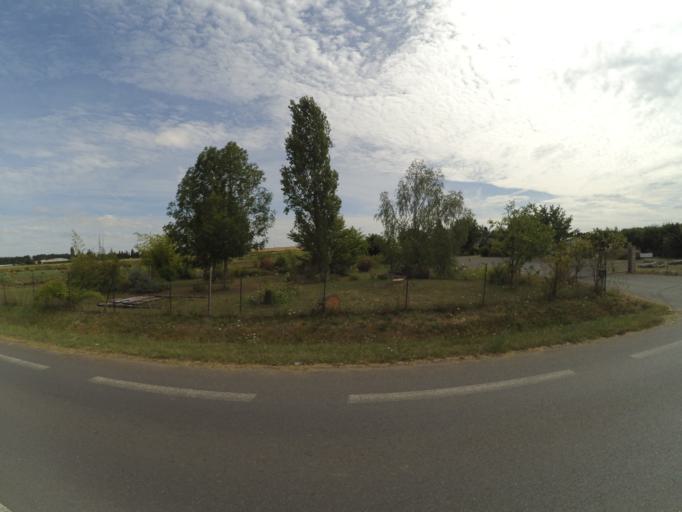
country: FR
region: Pays de la Loire
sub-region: Departement de Maine-et-Loire
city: Doue-la-Fontaine
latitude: 47.1881
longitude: -0.2871
